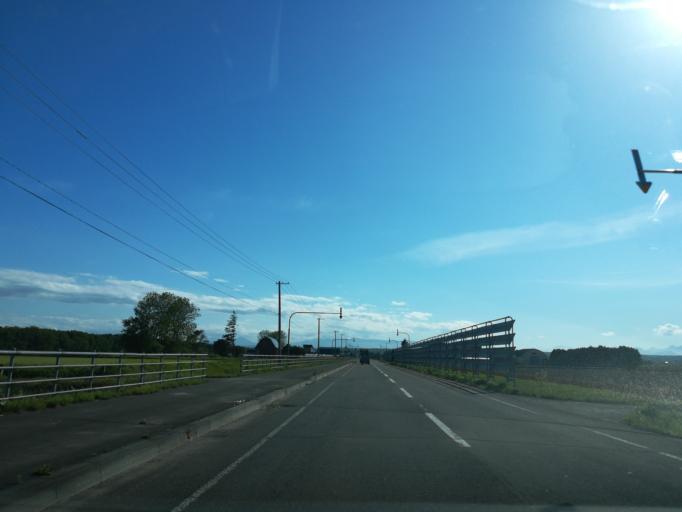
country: JP
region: Hokkaido
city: Kitahiroshima
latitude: 43.0455
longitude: 141.5939
